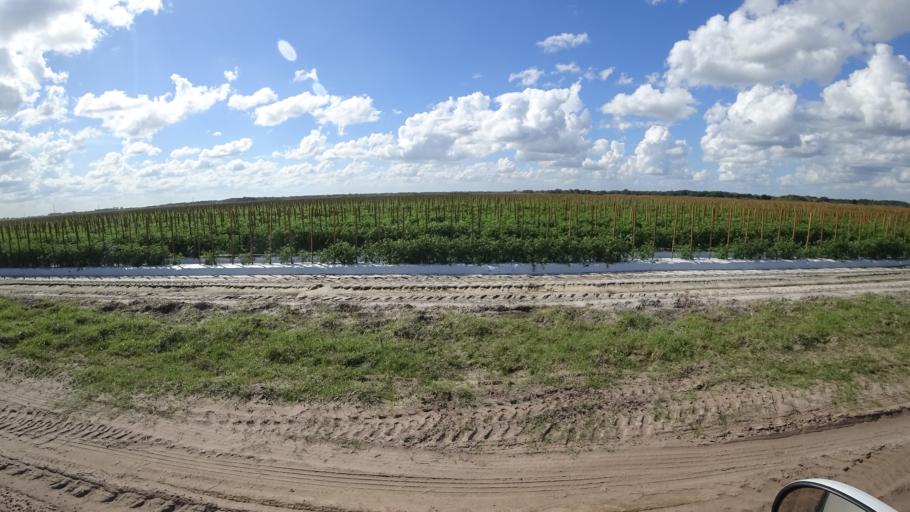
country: US
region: Florida
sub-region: DeSoto County
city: Arcadia
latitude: 27.3270
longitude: -82.0970
